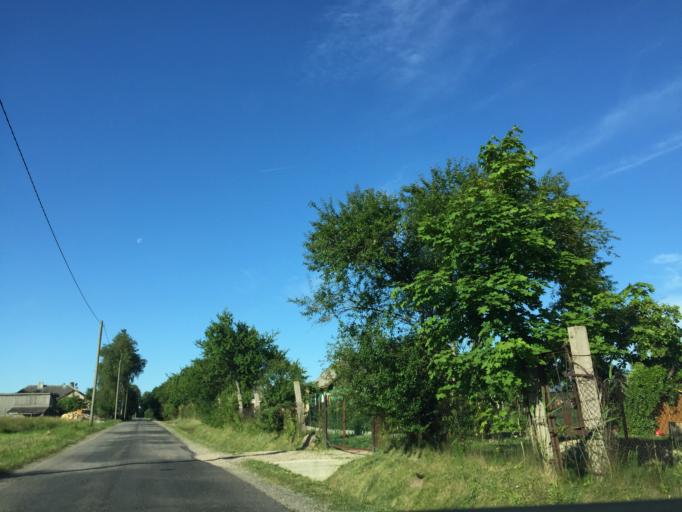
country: LV
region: Ventspils
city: Ventspils
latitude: 57.3689
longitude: 21.6087
